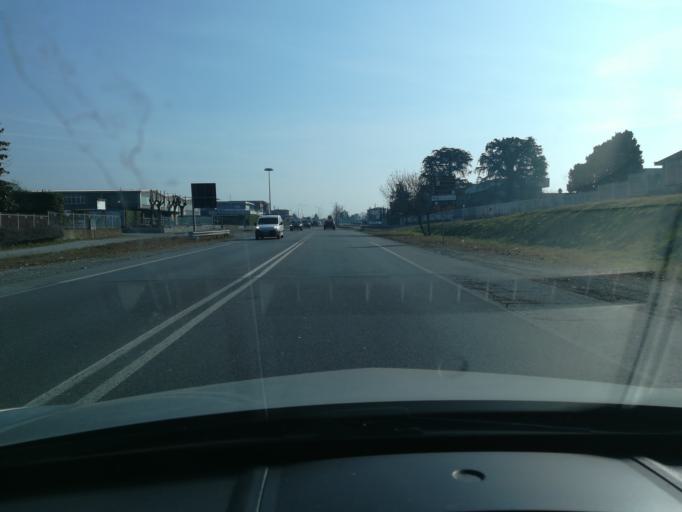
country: IT
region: Lombardy
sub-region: Provincia di Brescia
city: Palazzolo sull'Oglio
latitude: 45.5889
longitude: 9.8805
